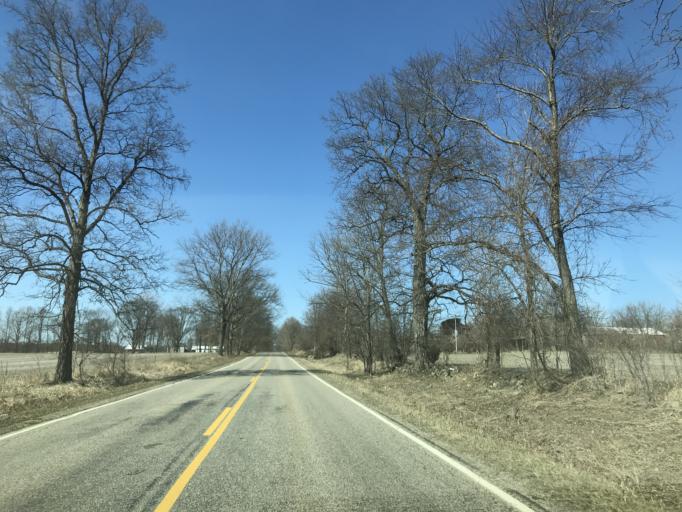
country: US
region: Michigan
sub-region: Hillsdale County
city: Litchfield
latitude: 41.9855
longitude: -84.7352
